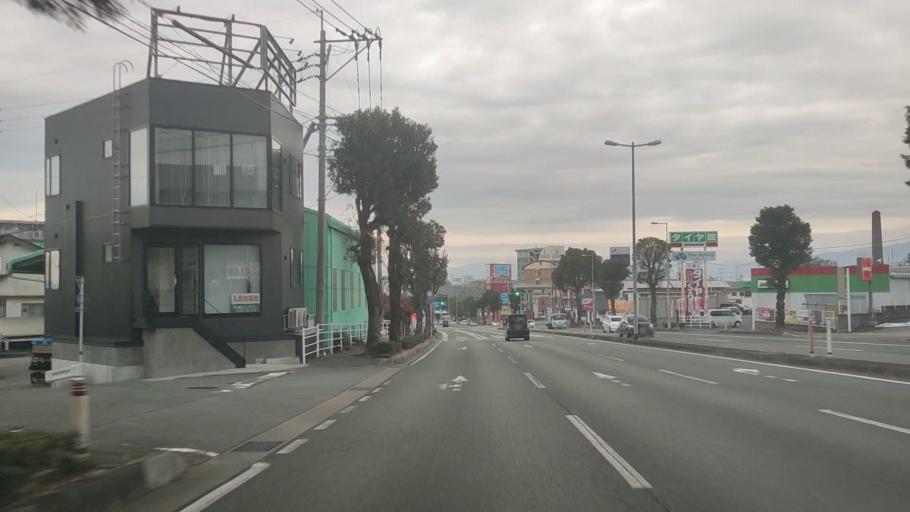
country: JP
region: Kumamoto
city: Ozu
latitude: 32.8393
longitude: 130.7796
